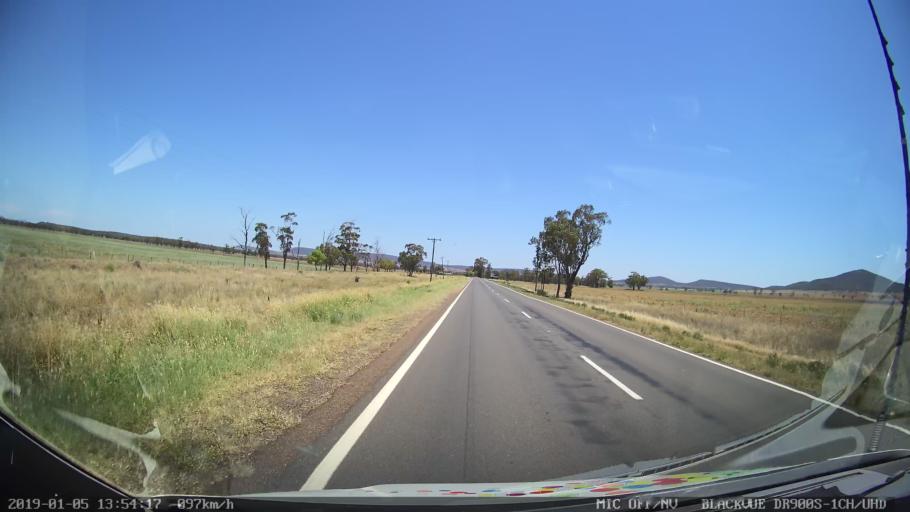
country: AU
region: New South Wales
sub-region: Gunnedah
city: Gunnedah
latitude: -31.0867
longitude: 150.2745
